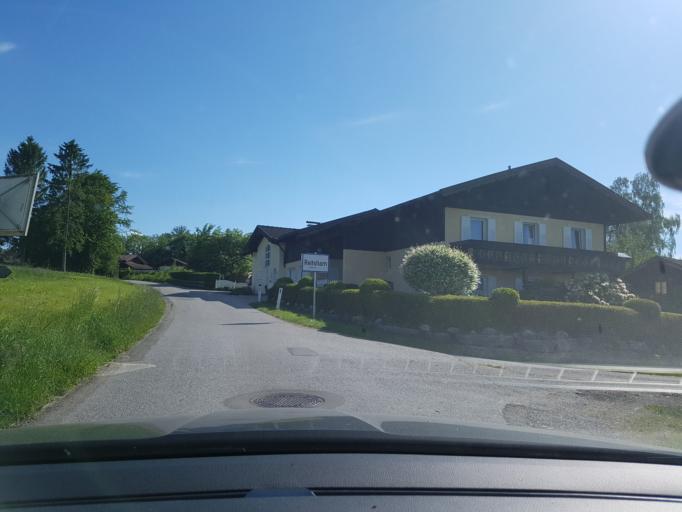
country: AT
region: Salzburg
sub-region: Politischer Bezirk Salzburg-Umgebung
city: Schleedorf
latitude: 47.9827
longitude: 13.1501
